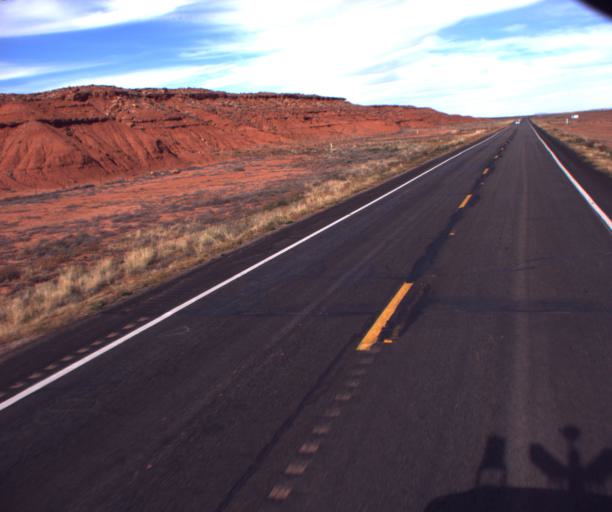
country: US
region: Arizona
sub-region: Navajo County
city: Kayenta
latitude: 36.9065
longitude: -109.7868
